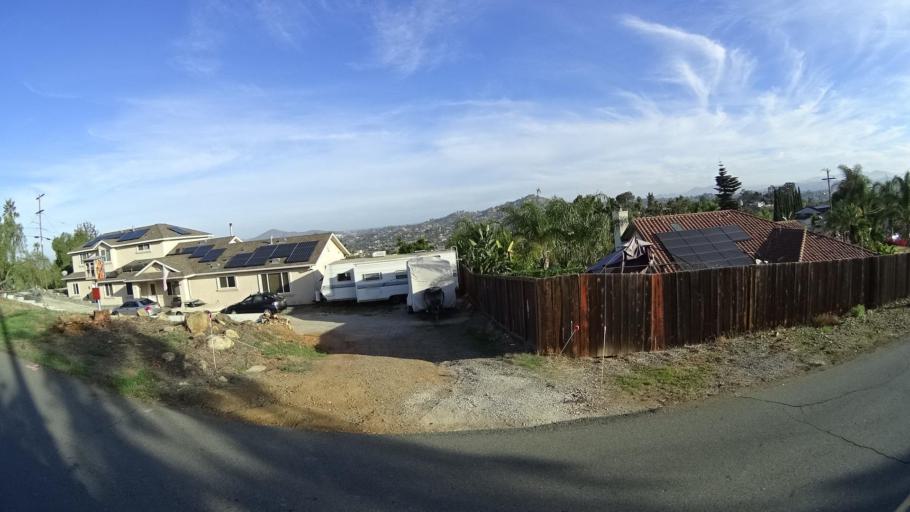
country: US
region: California
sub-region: San Diego County
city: Spring Valley
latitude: 32.7304
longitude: -116.9924
